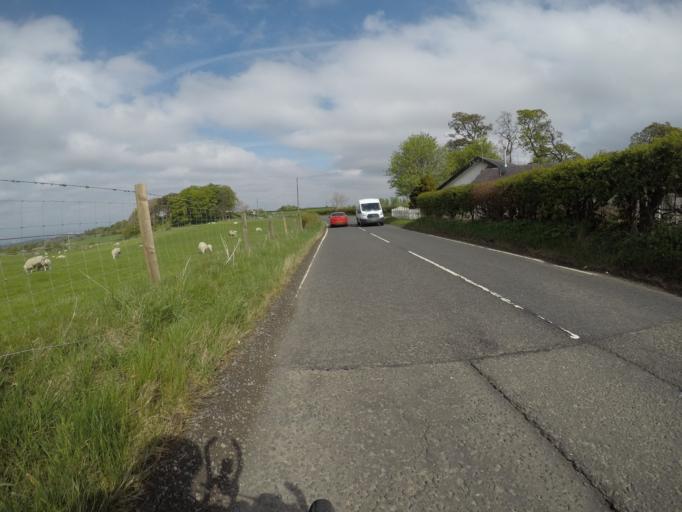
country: GB
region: Scotland
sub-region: East Renfrewshire
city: Newton Mearns
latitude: 55.7749
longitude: -4.3639
